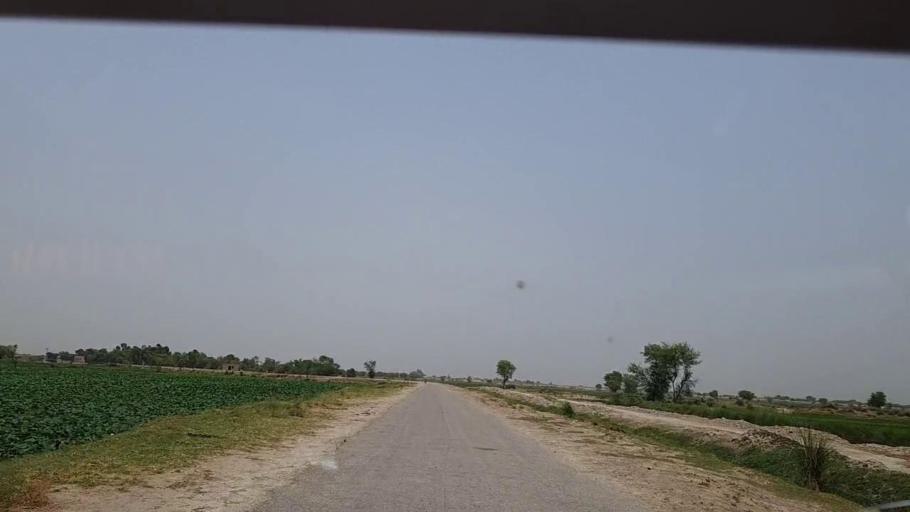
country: PK
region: Sindh
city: Khairpur Nathan Shah
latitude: 27.0124
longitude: 67.6705
